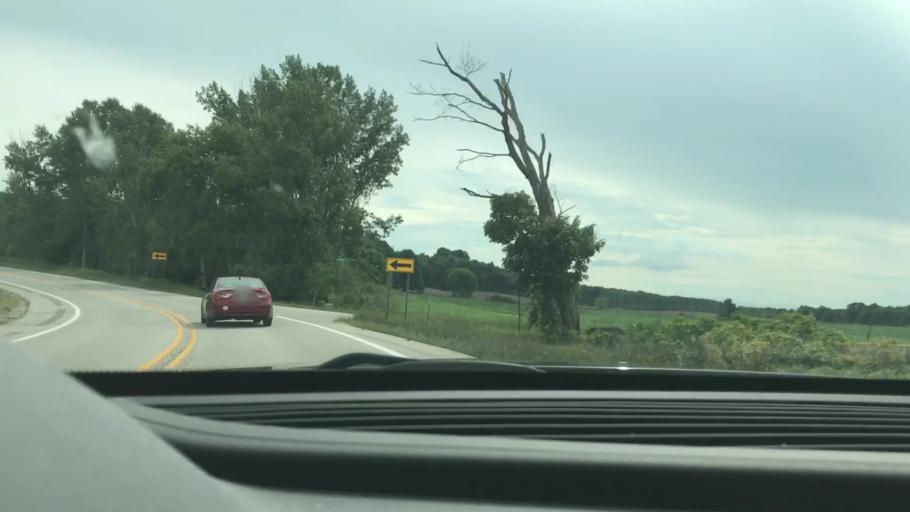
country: US
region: Michigan
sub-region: Antrim County
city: Bellaire
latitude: 45.0863
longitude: -85.2899
